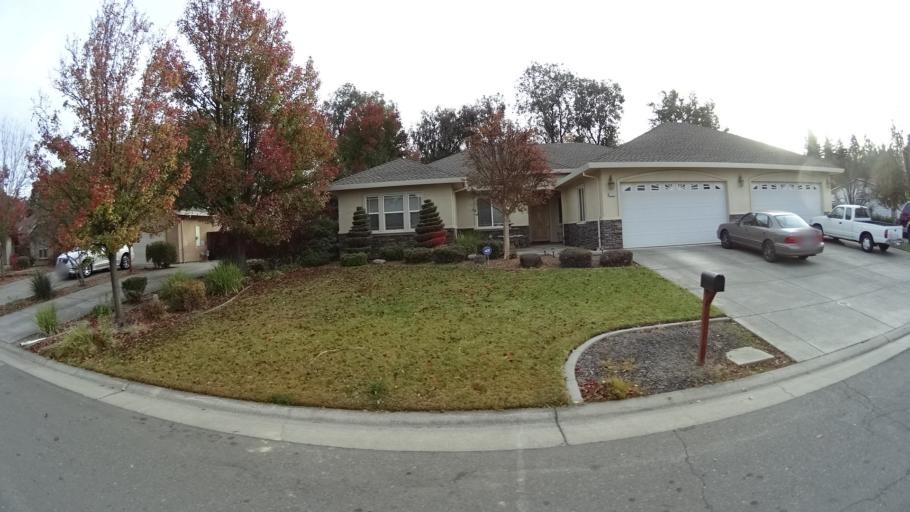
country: US
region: California
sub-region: Sacramento County
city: Citrus Heights
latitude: 38.7129
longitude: -121.2748
